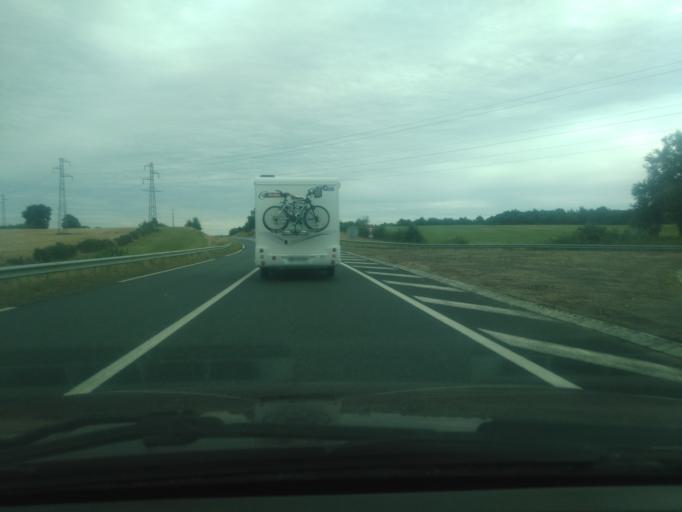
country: FR
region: Centre
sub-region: Departement de l'Indre
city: Saint-Marcel
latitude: 46.6044
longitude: 1.5299
